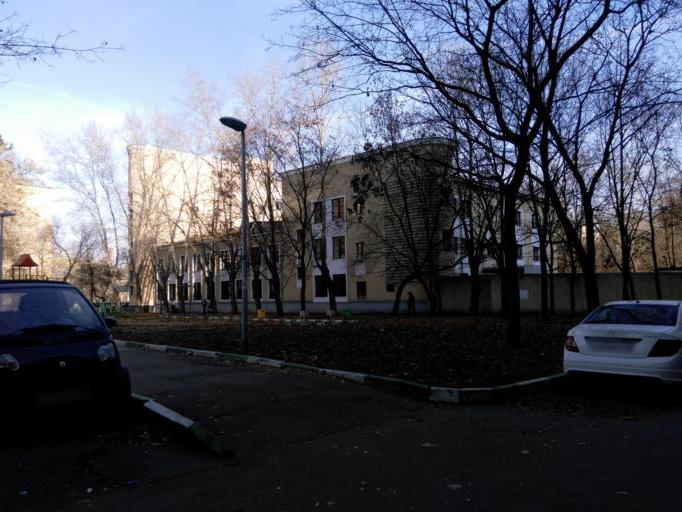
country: RU
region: Moscow
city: Novyye Cheremushki
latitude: 55.7070
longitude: 37.6132
